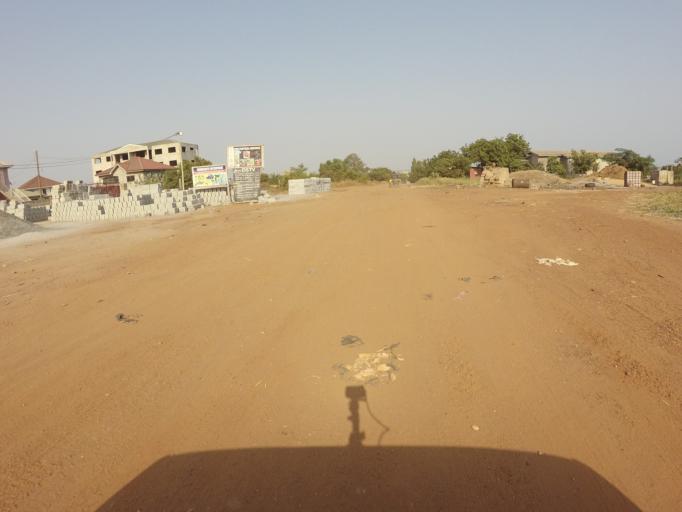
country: GH
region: Greater Accra
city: Tema
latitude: 5.7006
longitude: 0.0592
